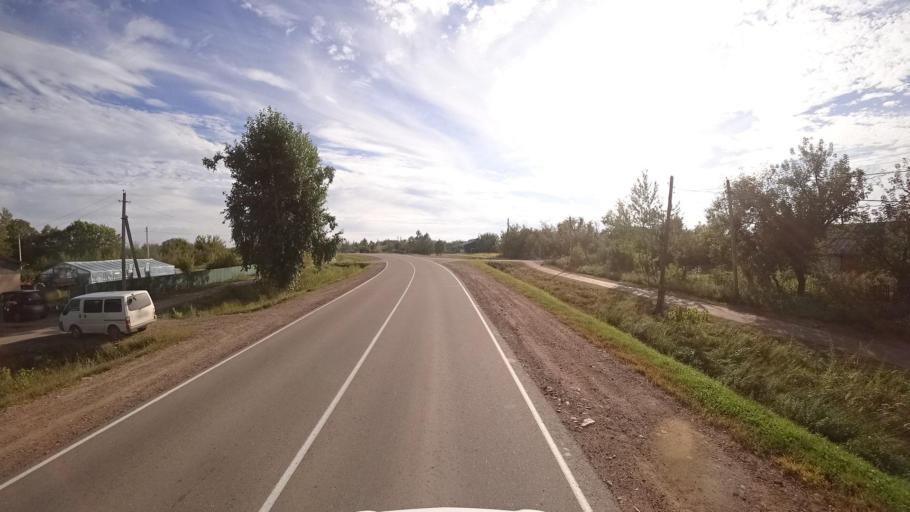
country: RU
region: Primorskiy
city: Dostoyevka
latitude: 44.3072
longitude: 133.4523
